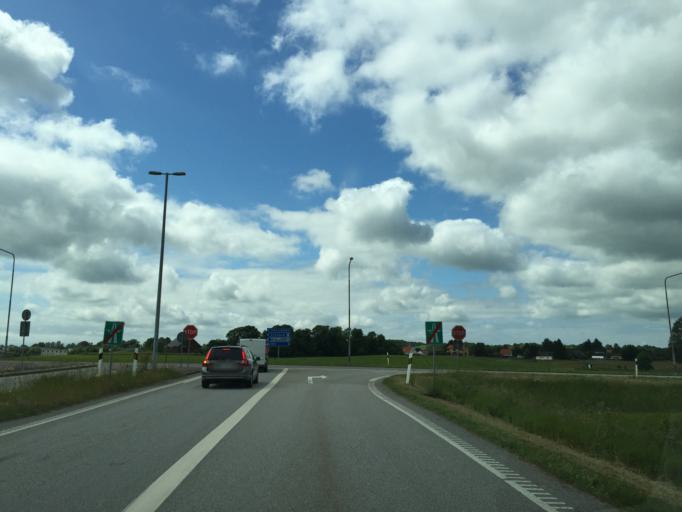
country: SE
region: Skane
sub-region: Svedala Kommun
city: Svedala
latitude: 55.5175
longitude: 13.2509
